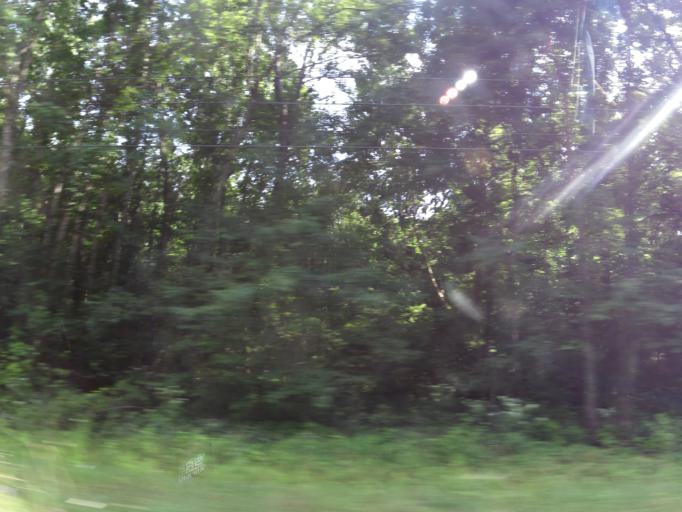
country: US
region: Tennessee
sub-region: Carroll County
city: Bruceton
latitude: 36.0354
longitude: -88.2152
